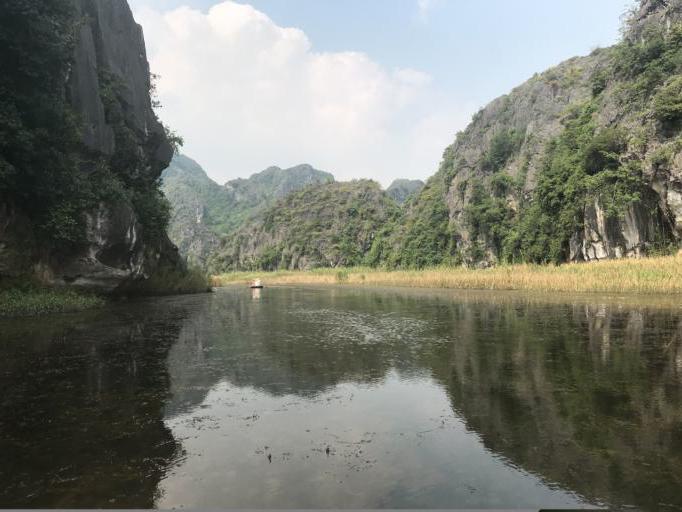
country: VN
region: Ninh Binh
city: Thi Tran Me
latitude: 20.3634
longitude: 105.8896
